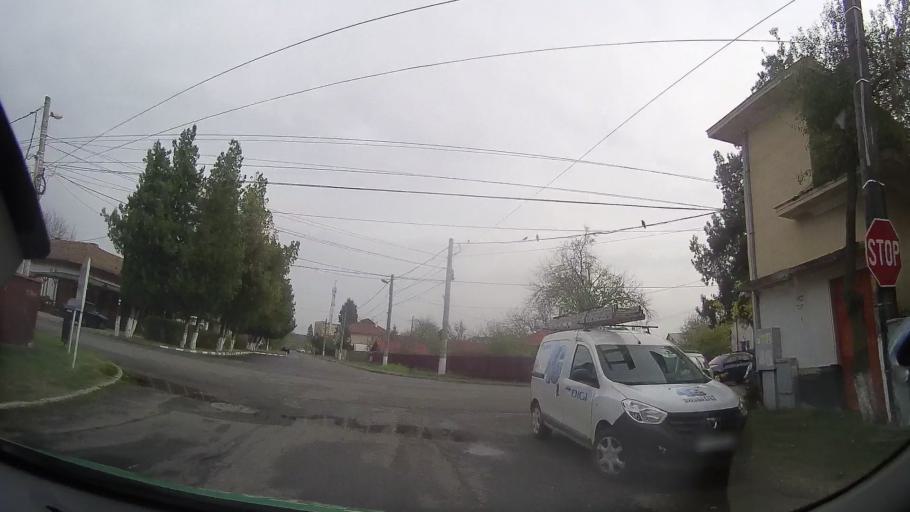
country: RO
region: Ilfov
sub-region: Comuna Snagov
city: Snagov
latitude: 44.7088
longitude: 26.1704
